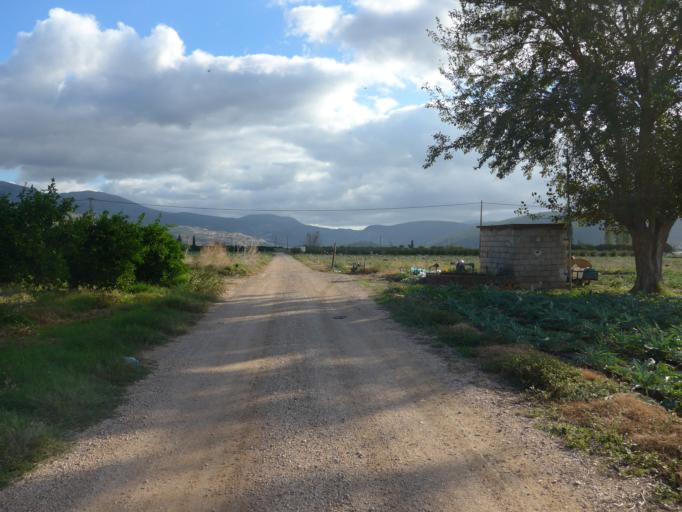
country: GR
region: Peloponnese
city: Asklipieio
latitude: 37.4905
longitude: 22.9960
